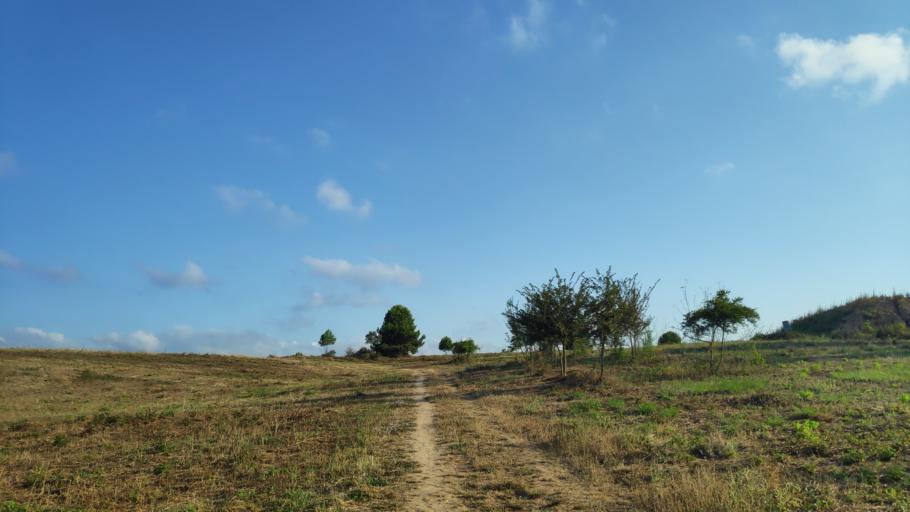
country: ES
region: Catalonia
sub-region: Provincia de Barcelona
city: Cerdanyola del Valles
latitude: 41.4922
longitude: 2.1189
